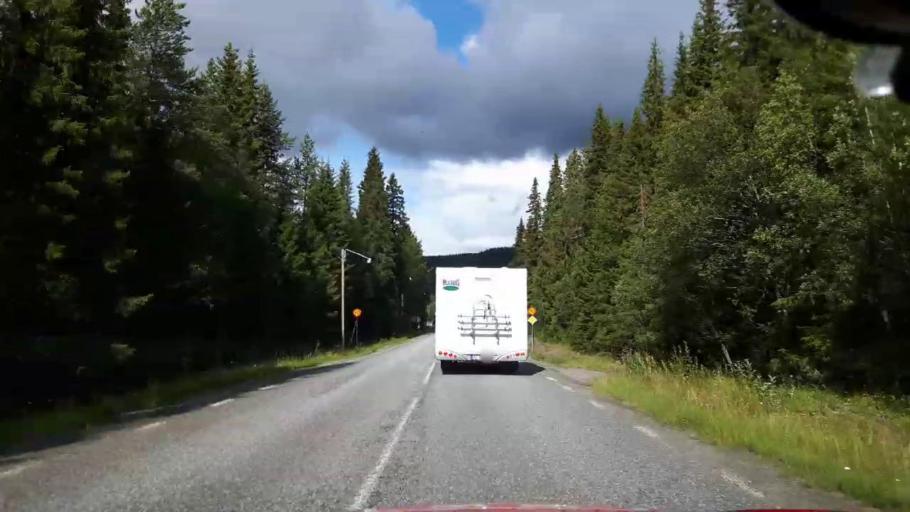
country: SE
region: Vaesterbotten
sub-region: Vilhelmina Kommun
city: Sjoberg
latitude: 64.9390
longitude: 15.8563
